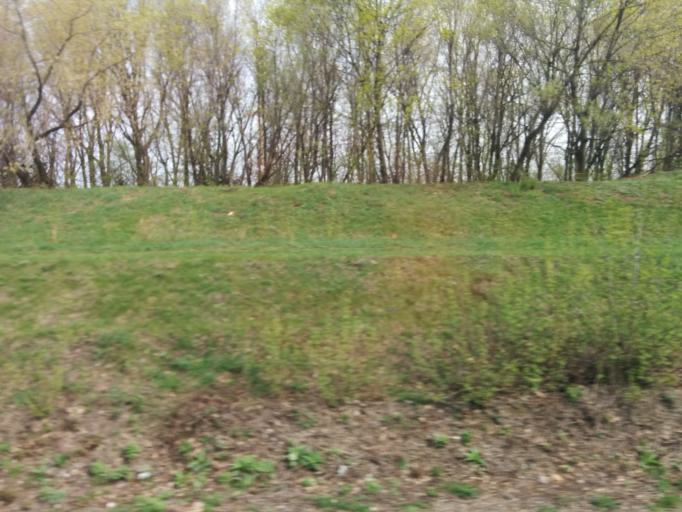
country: RU
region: Tambov
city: Tambov
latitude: 52.7542
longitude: 41.3899
